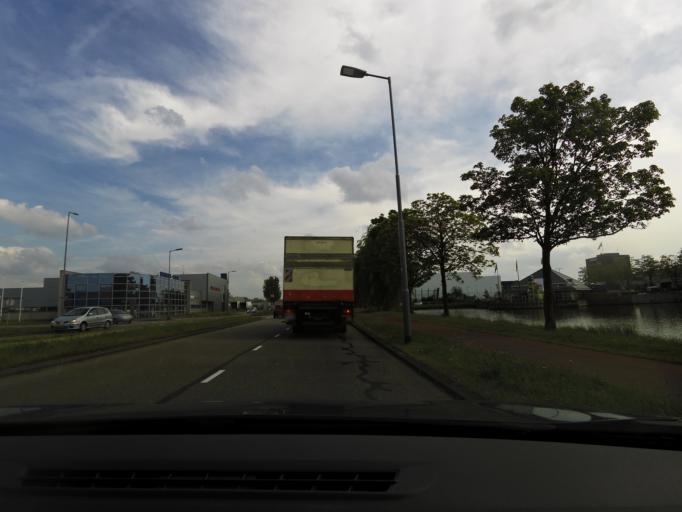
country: NL
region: South Holland
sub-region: Gemeente Schiedam
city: Schiedam
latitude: 51.9272
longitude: 4.4157
